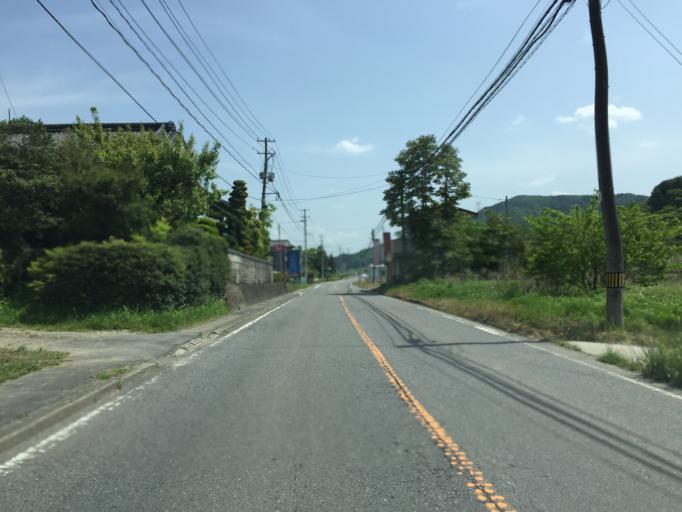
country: JP
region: Fukushima
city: Ishikawa
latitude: 37.1385
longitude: 140.4923
